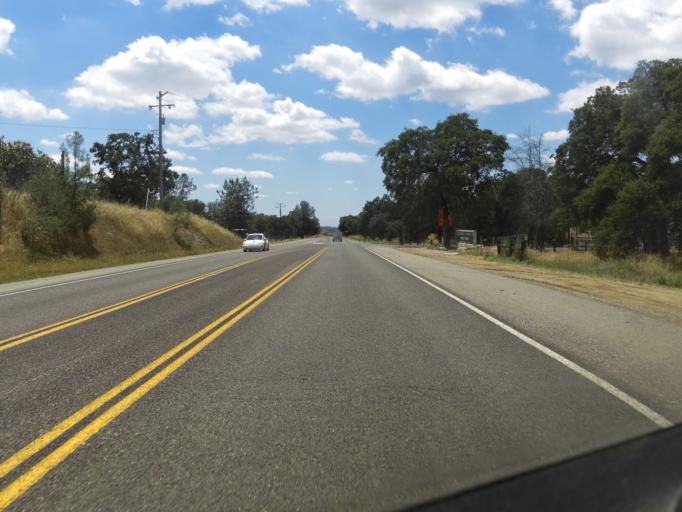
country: US
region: California
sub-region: Madera County
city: Yosemite Lakes
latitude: 37.1377
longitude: -119.6834
